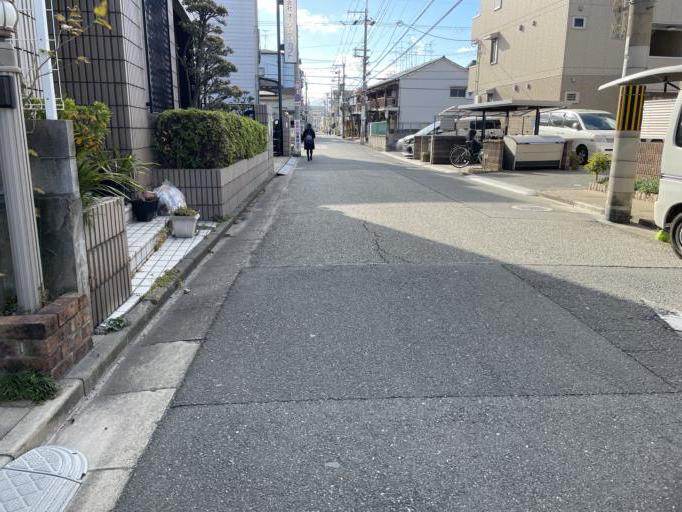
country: JP
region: Osaka
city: Daitocho
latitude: 34.6744
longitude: 135.5829
